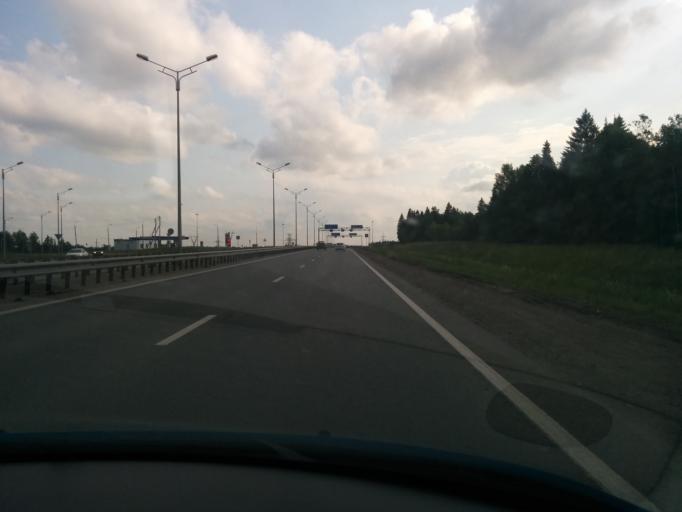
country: RU
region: Perm
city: Ferma
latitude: 58.0036
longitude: 56.3917
